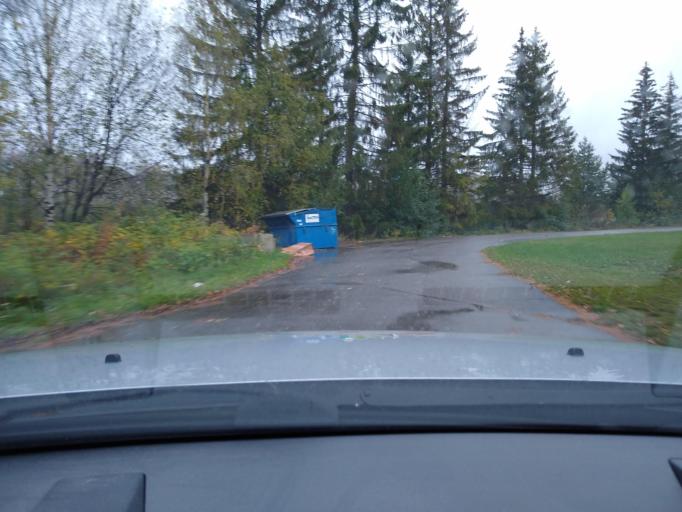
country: NO
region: Oppland
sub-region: Ringebu
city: Ringebu
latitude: 61.5410
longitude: 10.0530
